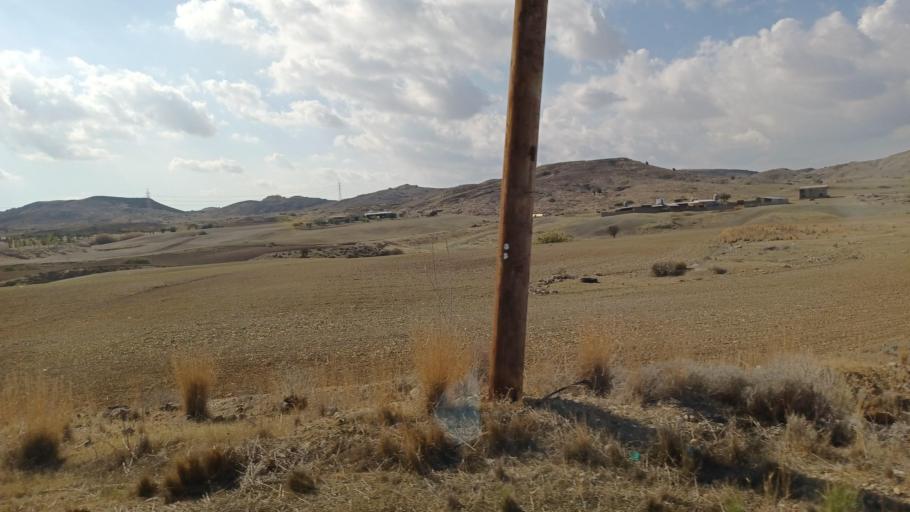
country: CY
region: Larnaka
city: Voroklini
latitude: 35.0096
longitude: 33.6431
